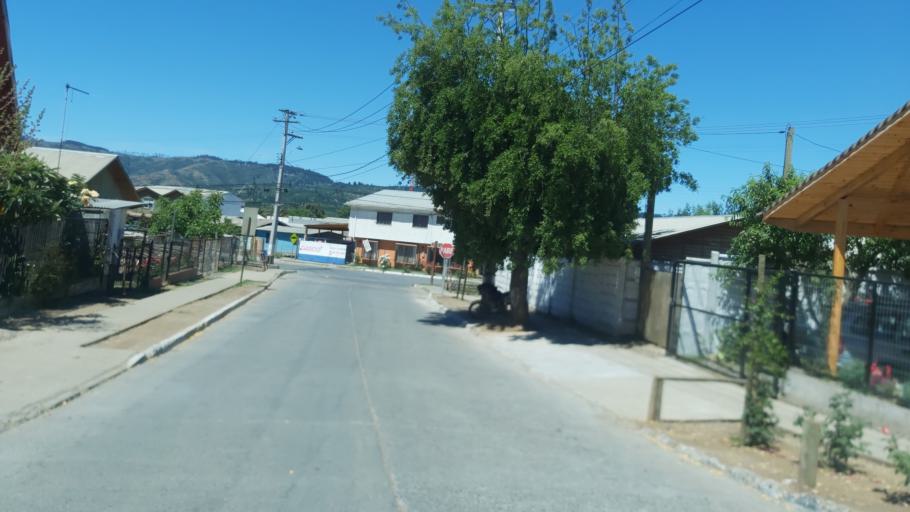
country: CL
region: Maule
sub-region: Provincia de Talca
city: Talca
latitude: -34.9847
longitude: -71.9829
